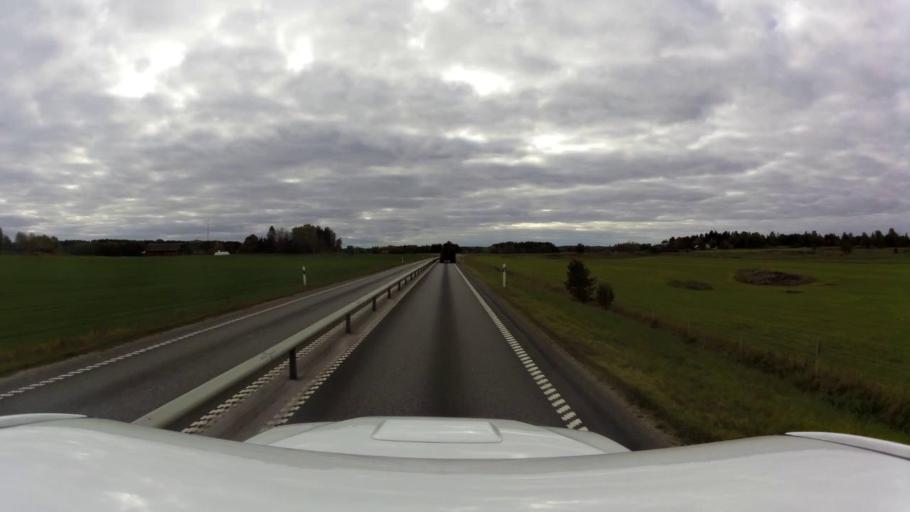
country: SE
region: OEstergoetland
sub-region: Linkopings Kommun
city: Malmslatt
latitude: 58.3335
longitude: 15.5595
